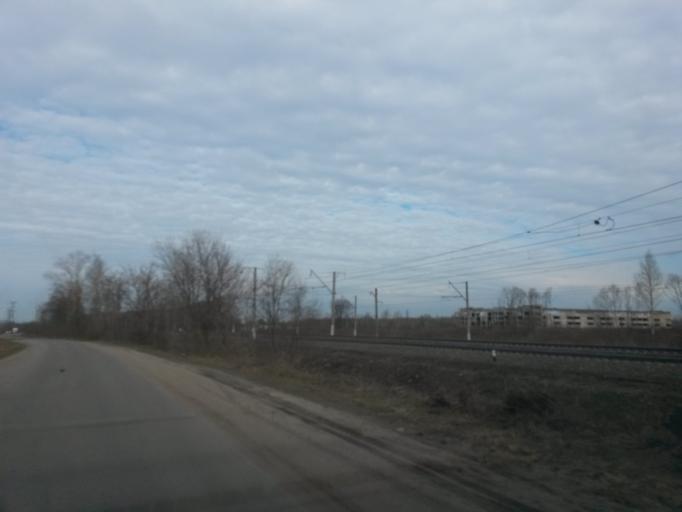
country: RU
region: Jaroslavl
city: Yaroslavl
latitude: 57.6441
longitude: 39.8231
